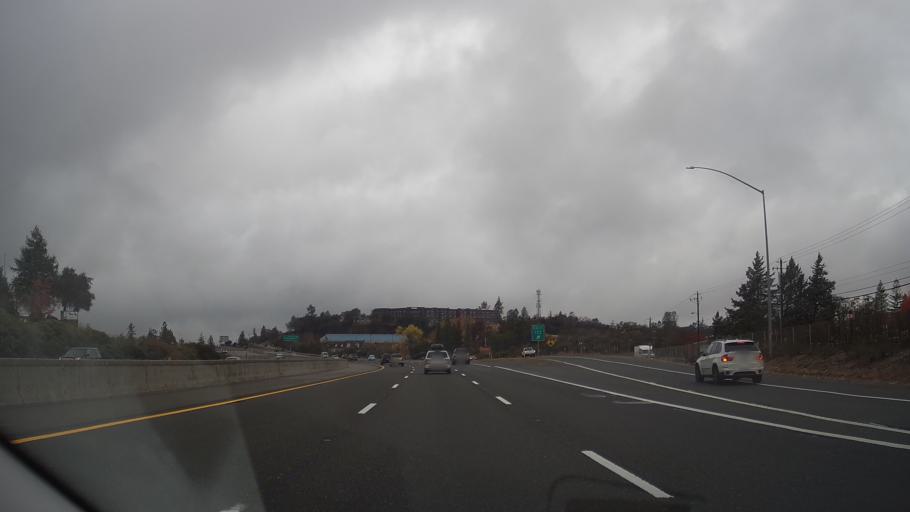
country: US
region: California
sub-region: Placer County
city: North Auburn
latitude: 38.9362
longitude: -121.0538
